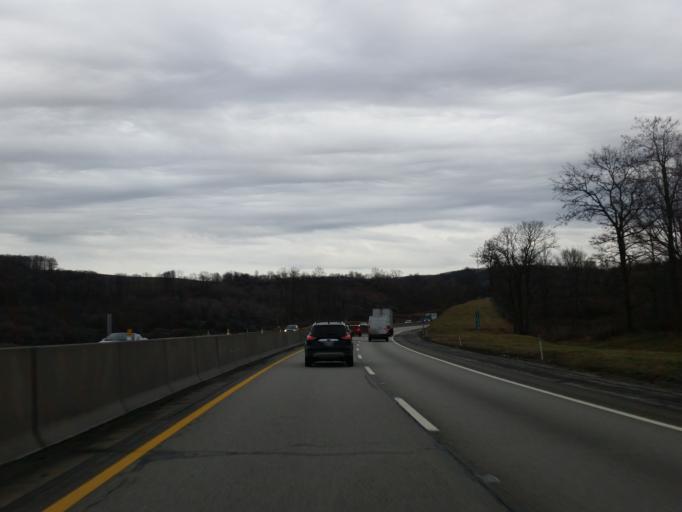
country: US
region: Pennsylvania
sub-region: Somerset County
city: Somerset
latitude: 40.0749
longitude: -79.1635
